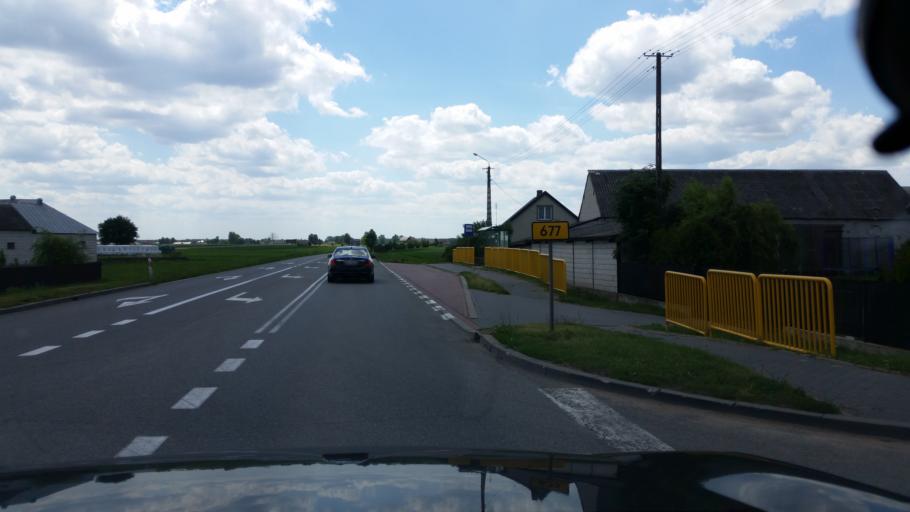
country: PL
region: Masovian Voivodeship
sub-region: Powiat ostrolecki
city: Czerwin
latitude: 52.9378
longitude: 21.8845
